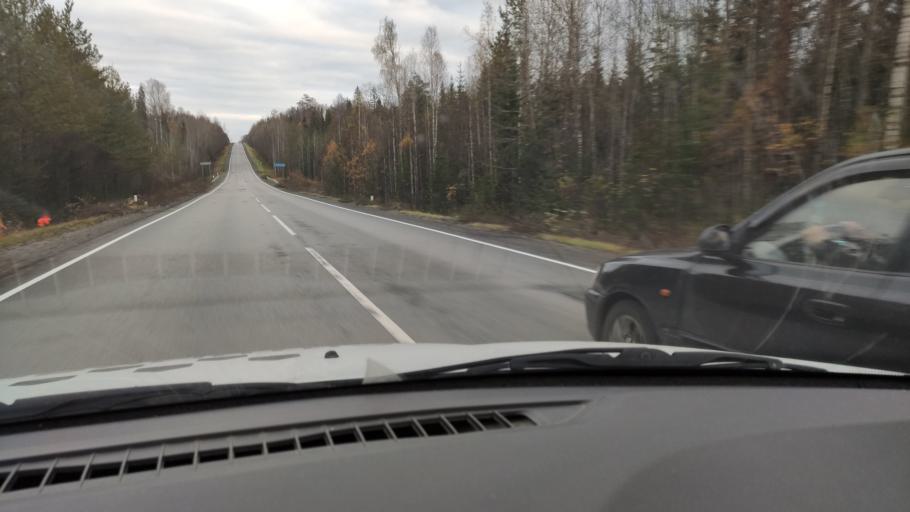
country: RU
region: Kirov
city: Chernaya Kholunitsa
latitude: 58.8650
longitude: 51.5811
